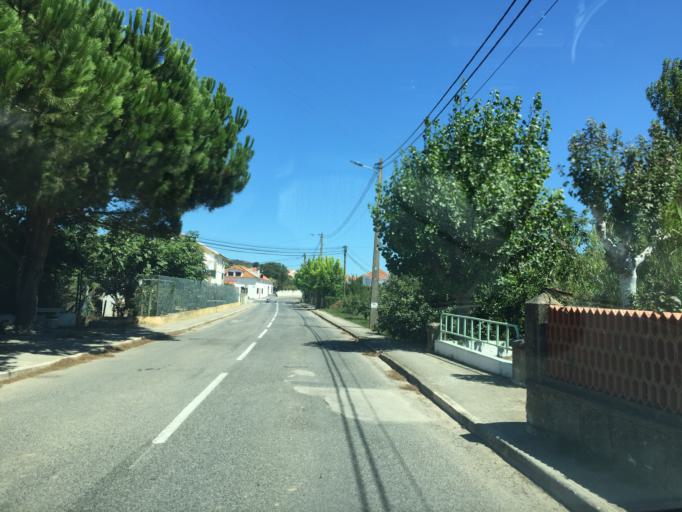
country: PT
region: Lisbon
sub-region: Torres Vedras
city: A dos Cunhados
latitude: 39.1798
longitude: -9.3164
